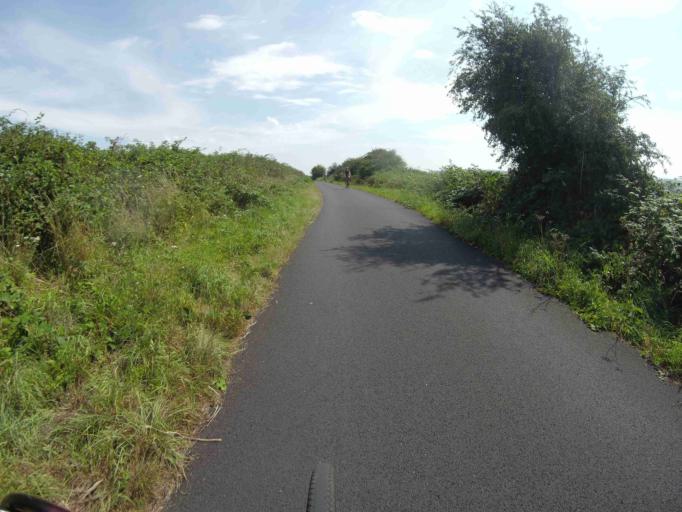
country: GB
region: England
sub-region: Devon
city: Topsham
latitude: 50.6843
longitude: -3.4783
